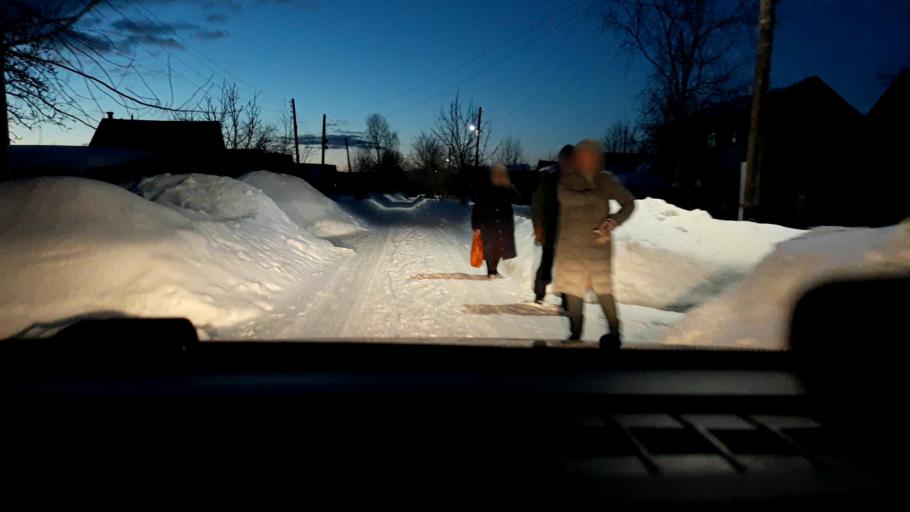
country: RU
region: Nizjnij Novgorod
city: Lukino
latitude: 56.4181
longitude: 43.6511
